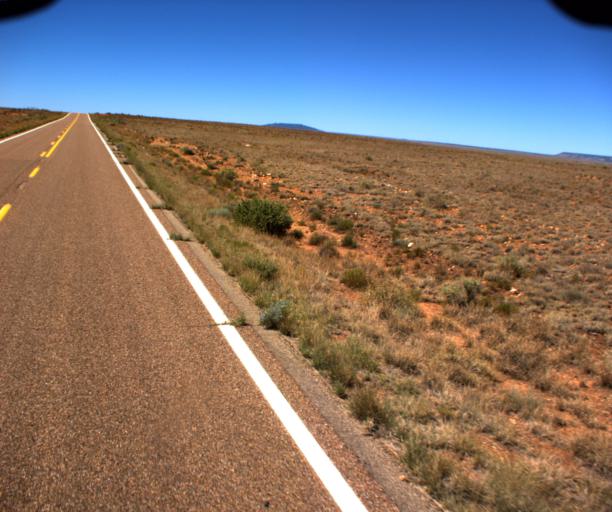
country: US
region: Arizona
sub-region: Navajo County
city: Winslow
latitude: 34.8661
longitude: -110.6589
